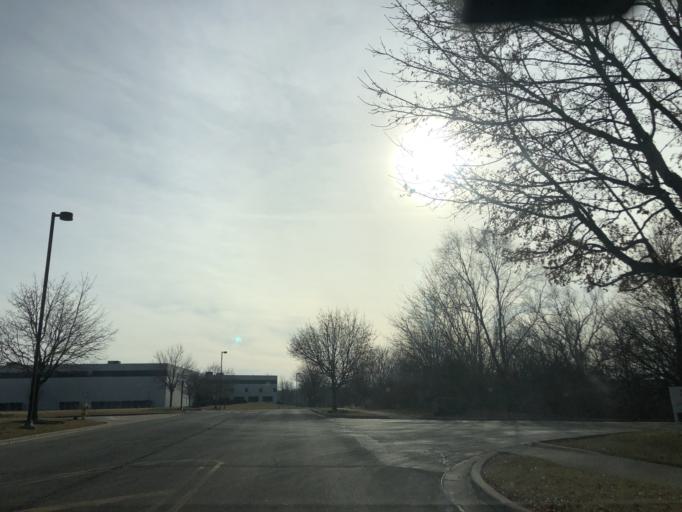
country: US
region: Illinois
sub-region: Cook County
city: Lemont
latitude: 41.6985
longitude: -88.0249
